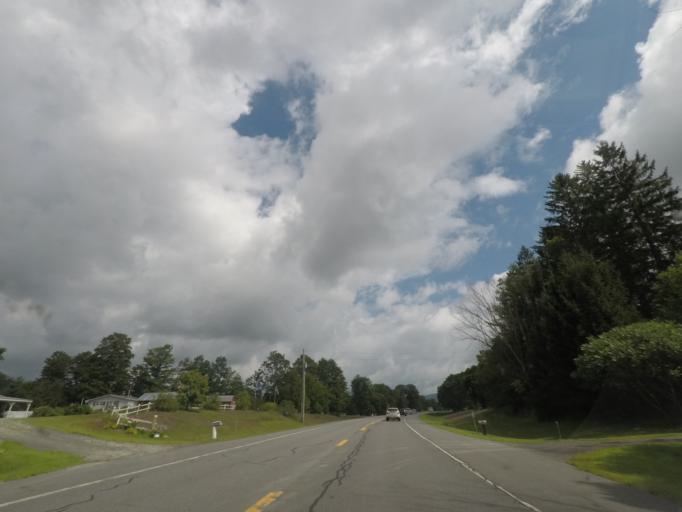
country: US
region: Massachusetts
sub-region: Berkshire County
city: Lanesborough
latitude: 42.5592
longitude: -73.3736
